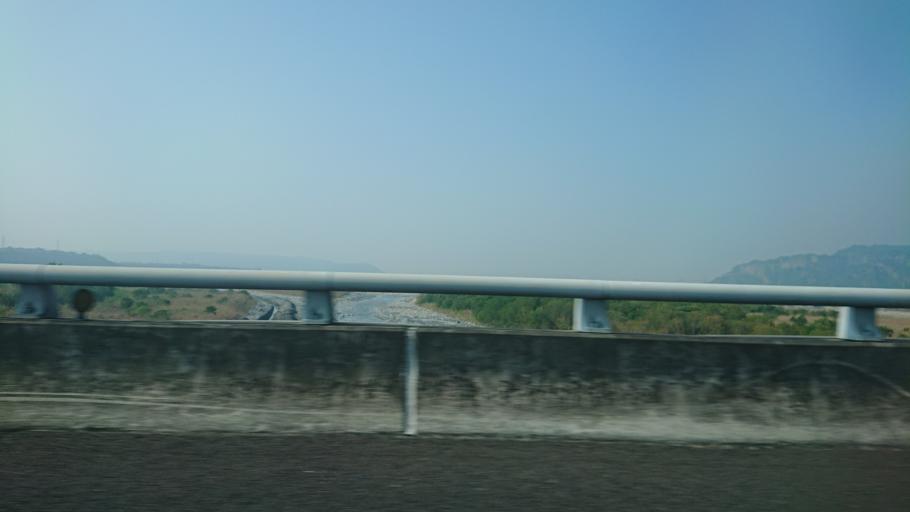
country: TW
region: Taiwan
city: Lugu
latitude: 23.8019
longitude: 120.6988
